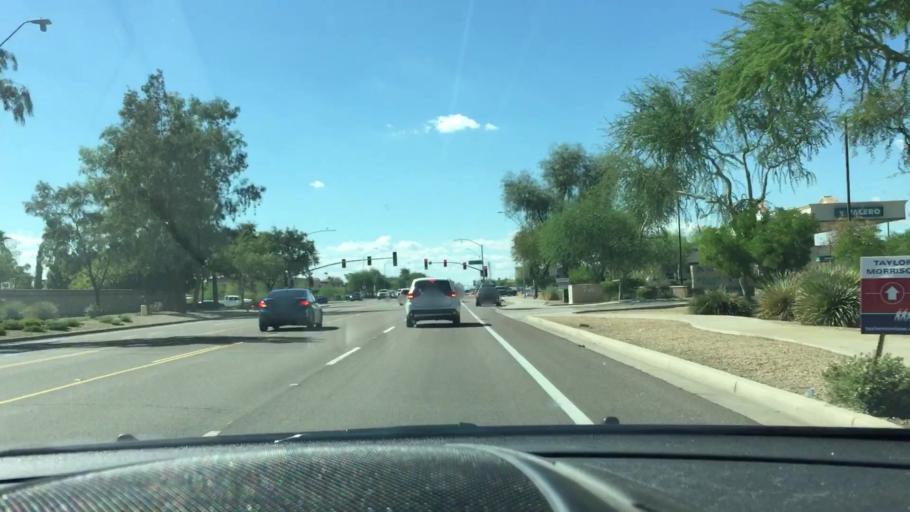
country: US
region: Arizona
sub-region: Maricopa County
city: Sun City
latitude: 33.6817
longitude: -112.2363
